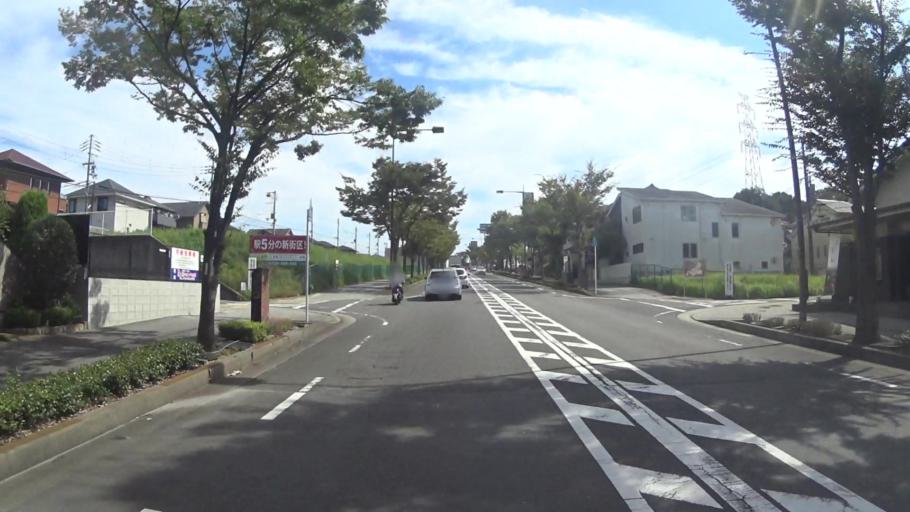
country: JP
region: Kyoto
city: Yawata
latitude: 34.8381
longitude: 135.7164
